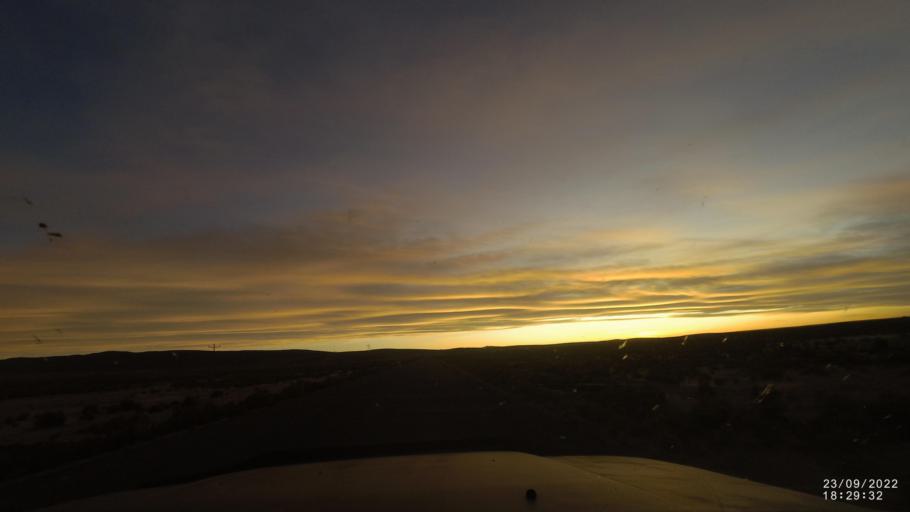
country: BO
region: Oruro
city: Challapata
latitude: -19.3458
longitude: -67.1933
